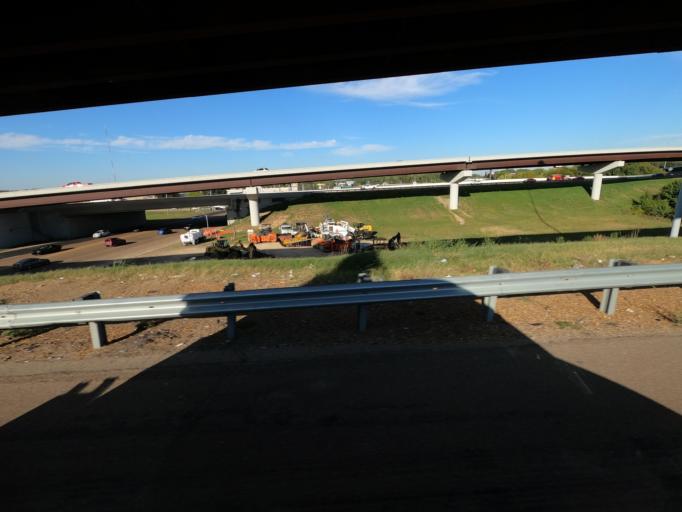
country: US
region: Tennessee
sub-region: Shelby County
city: Bartlett
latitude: 35.1531
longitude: -89.8875
